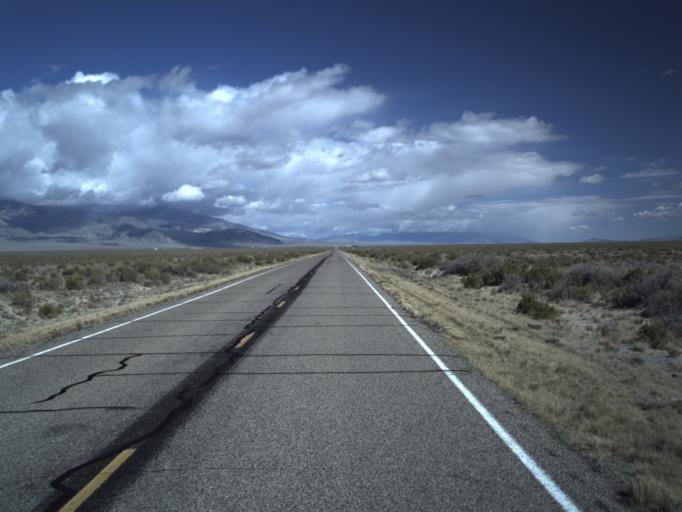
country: US
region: Nevada
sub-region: White Pine County
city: McGill
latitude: 38.9963
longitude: -114.0346
